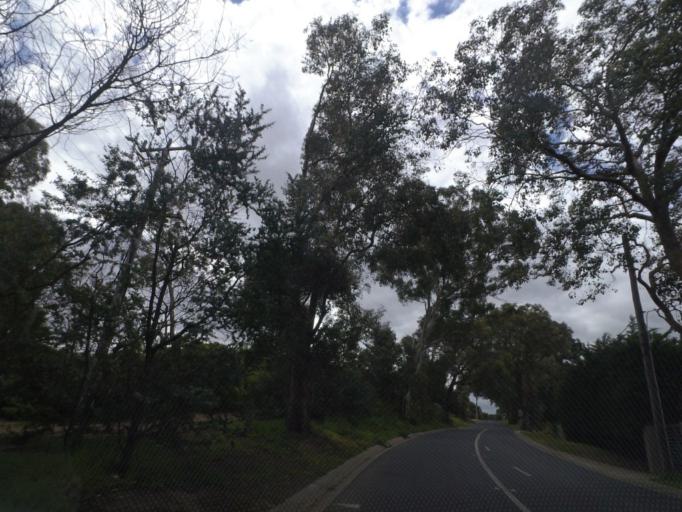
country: AU
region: Victoria
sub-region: Nillumbik
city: Diamond Creek
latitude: -37.6588
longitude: 145.1599
